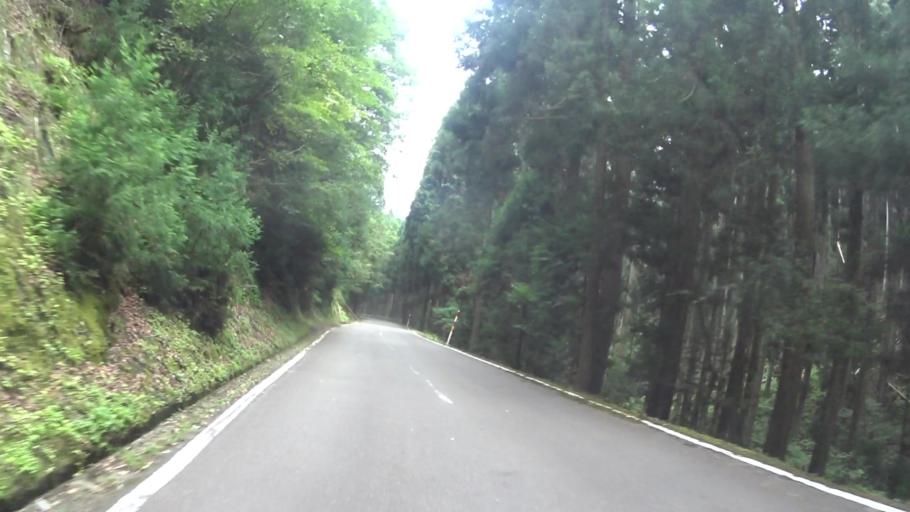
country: JP
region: Kyoto
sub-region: Kyoto-shi
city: Kamigyo-ku
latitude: 35.2026
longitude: 135.6767
